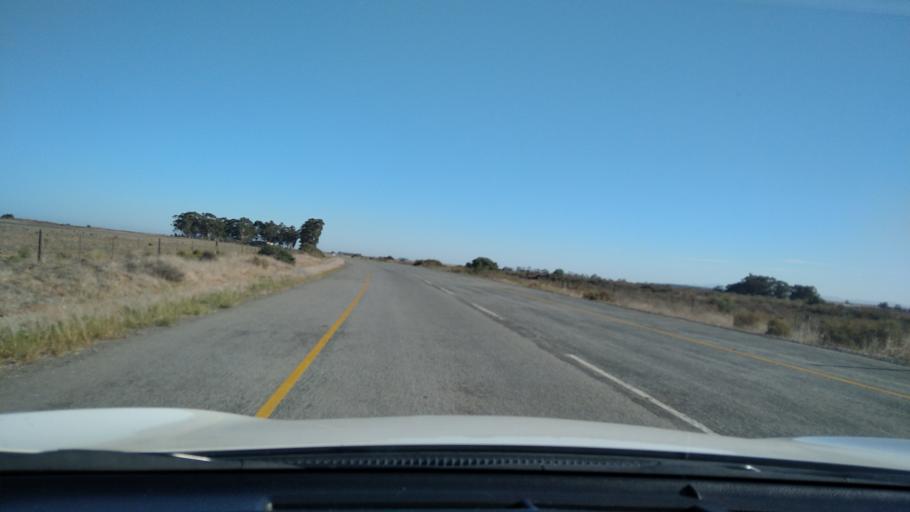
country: ZA
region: Western Cape
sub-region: West Coast District Municipality
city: Moorreesburg
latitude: -33.2673
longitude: 18.5980
